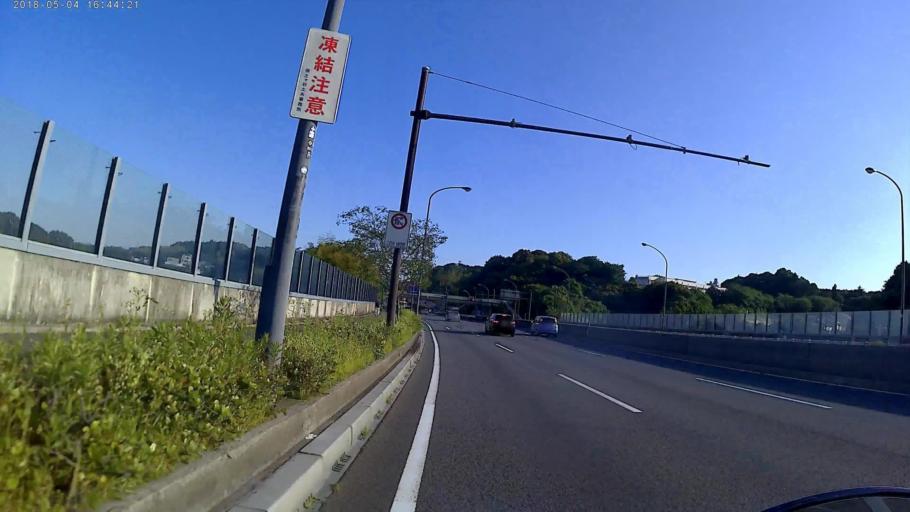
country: JP
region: Kanagawa
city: Yokohama
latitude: 35.4493
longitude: 139.5604
